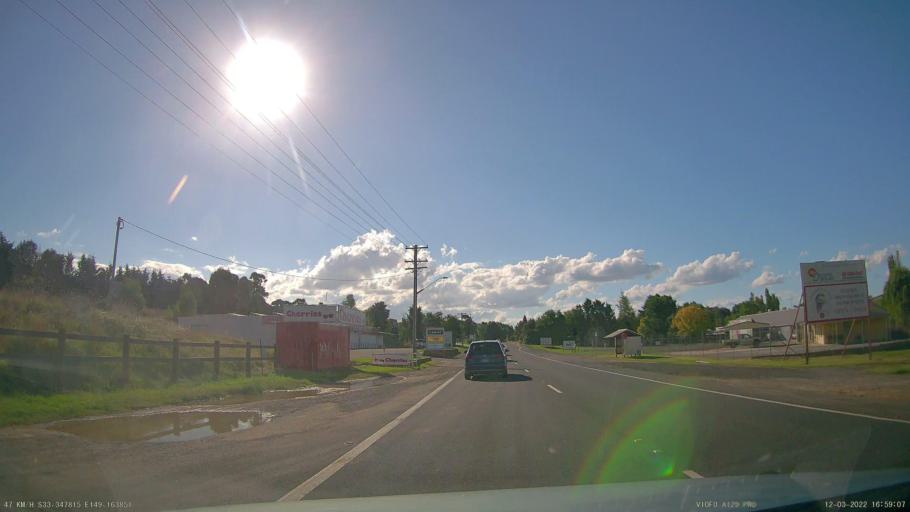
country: AU
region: New South Wales
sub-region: Orange Municipality
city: Orange
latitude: -33.3477
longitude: 149.1637
